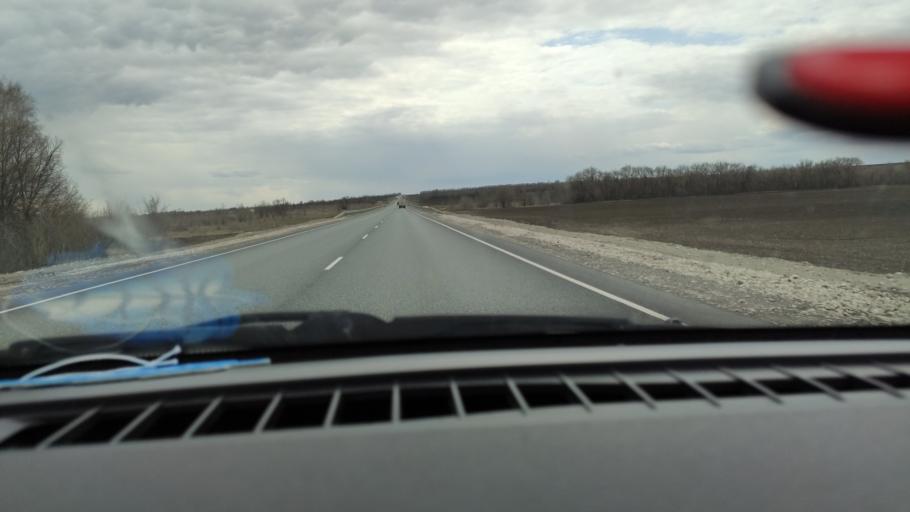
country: RU
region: Saratov
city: Yelshanka
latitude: 51.8490
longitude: 46.4867
